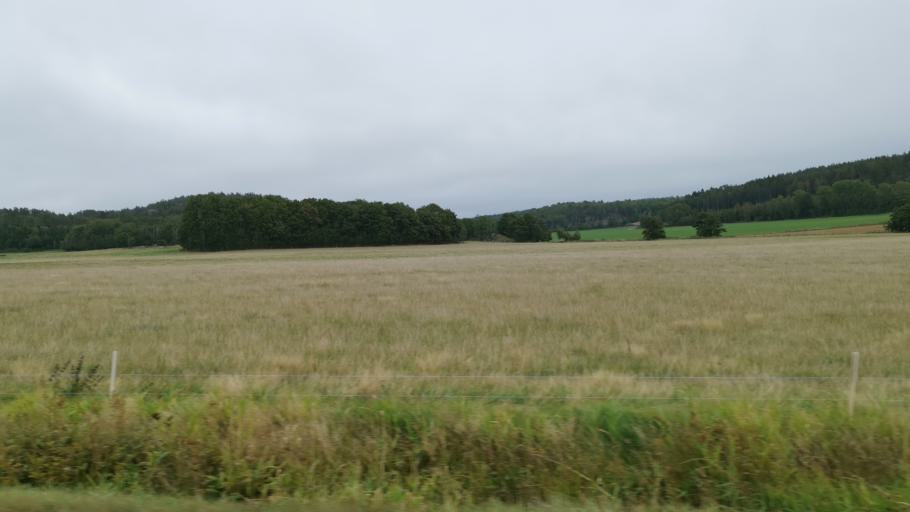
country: SE
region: Vaestra Goetaland
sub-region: Tanums Kommun
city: Tanumshede
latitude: 58.5987
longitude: 11.3670
